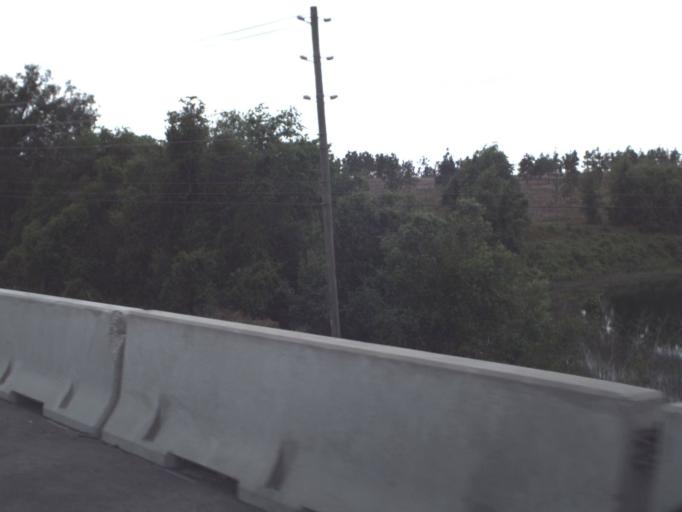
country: US
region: Florida
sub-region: Lake County
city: Clermont
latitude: 28.4446
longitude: -81.7185
